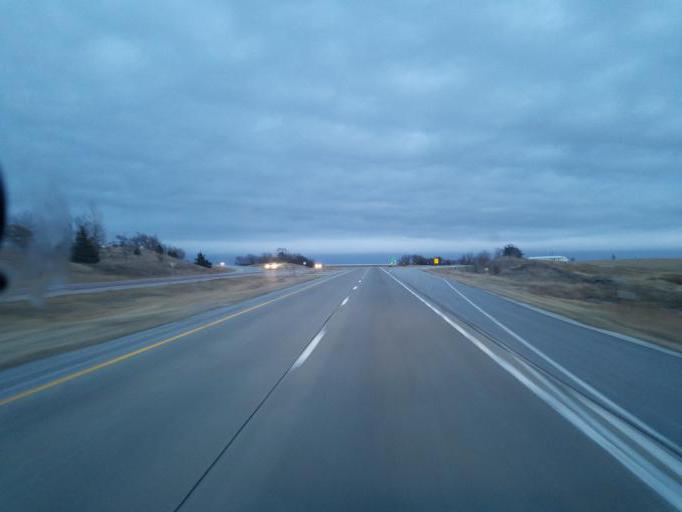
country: US
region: Iowa
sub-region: Cass County
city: Atlantic
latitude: 41.4978
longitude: -95.1240
